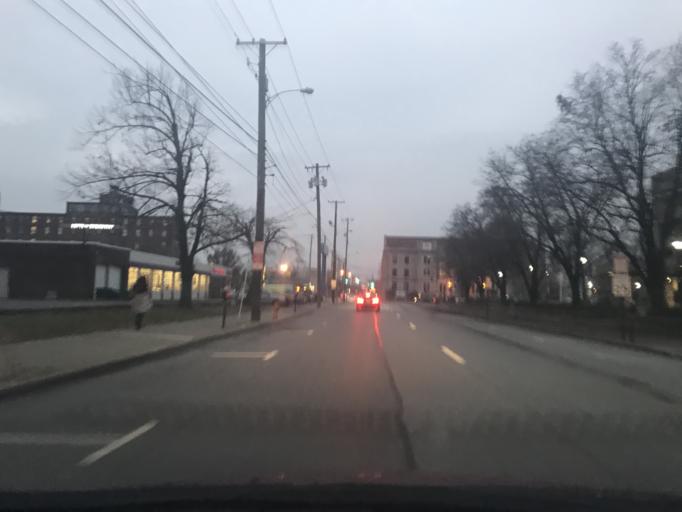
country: US
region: Kentucky
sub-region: Jefferson County
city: Louisville
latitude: 38.2464
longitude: -85.7475
